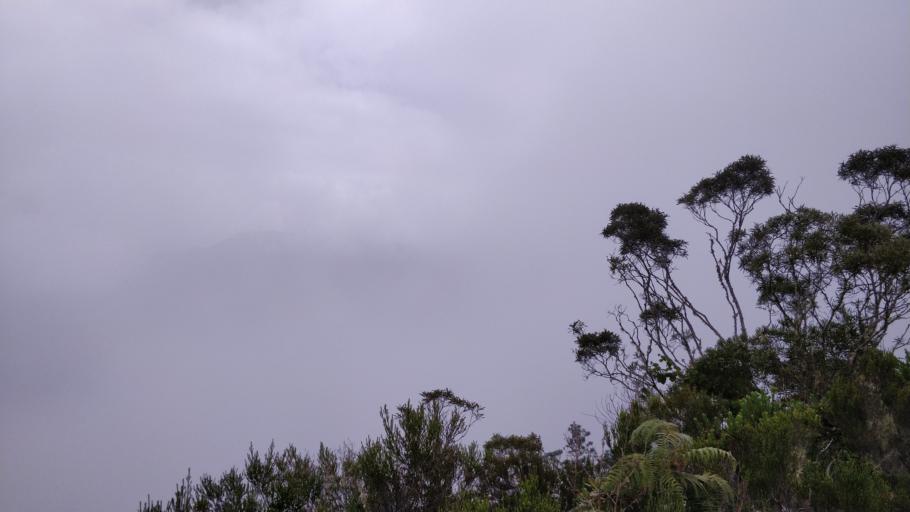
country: RE
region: Reunion
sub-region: Reunion
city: Salazie
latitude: -21.0646
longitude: 55.5322
